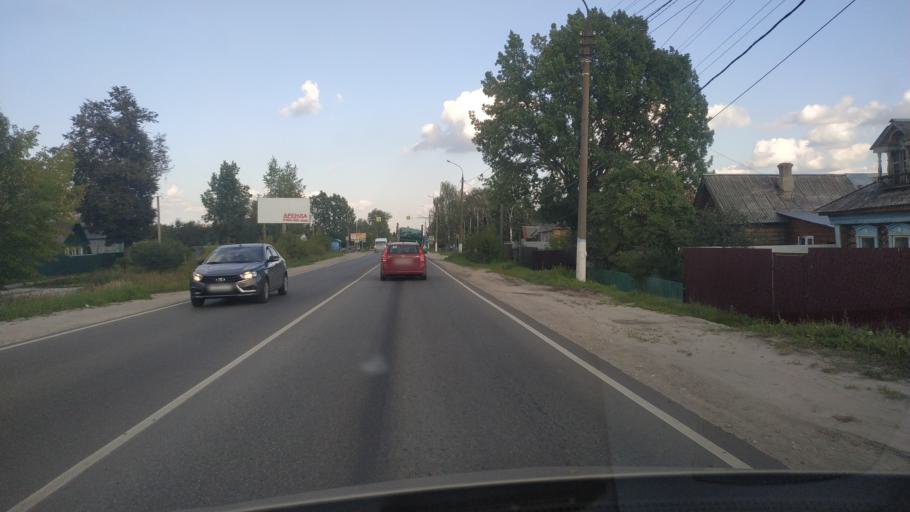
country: RU
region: Moskovskaya
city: Shatura
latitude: 55.5774
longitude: 39.4914
